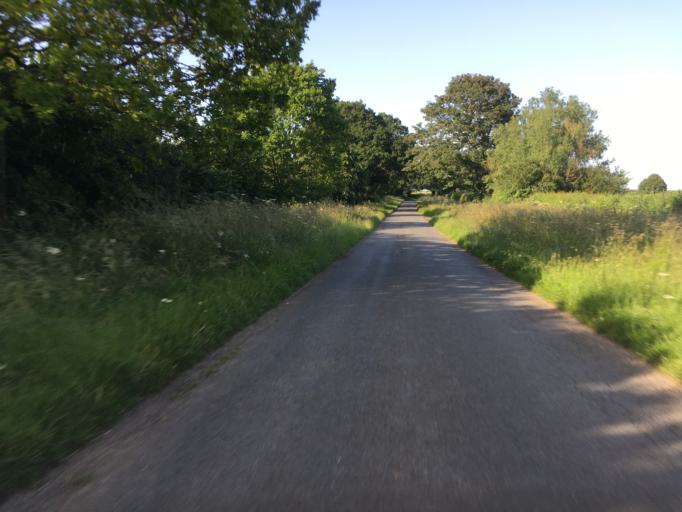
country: GB
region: England
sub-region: Gloucestershire
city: Fairford
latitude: 51.7287
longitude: -1.7535
